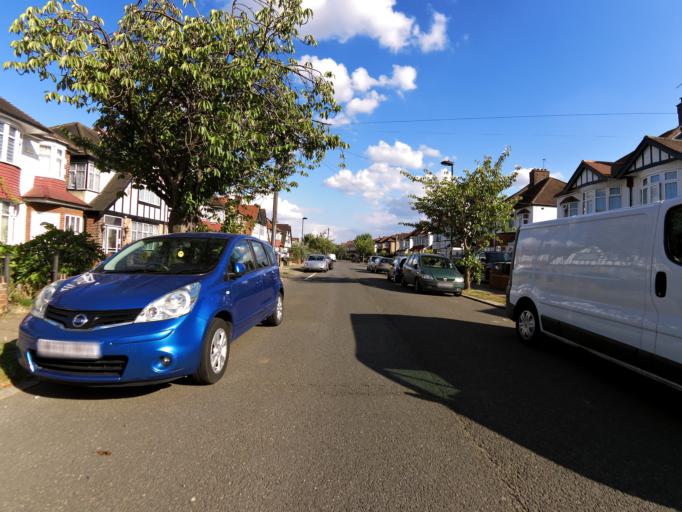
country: GB
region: England
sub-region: Greater London
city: Wood Green
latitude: 51.6163
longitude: -0.1243
